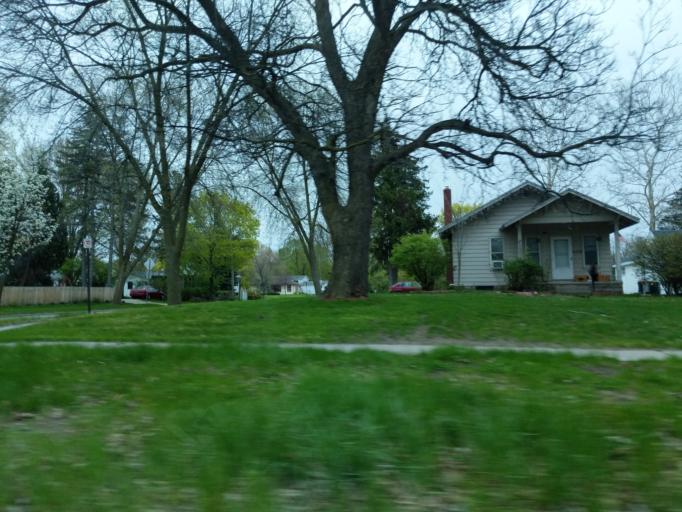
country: US
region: Michigan
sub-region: Midland County
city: Midland
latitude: 43.6302
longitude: -84.2270
